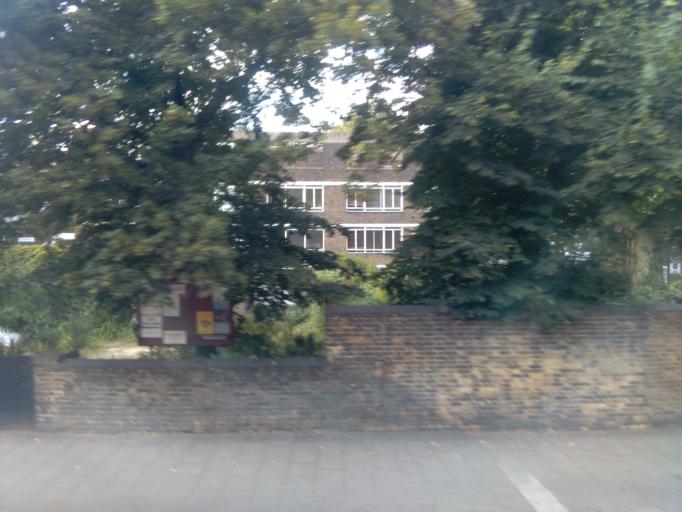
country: GB
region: England
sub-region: Greater London
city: Camberwell
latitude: 51.4737
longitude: -0.0869
